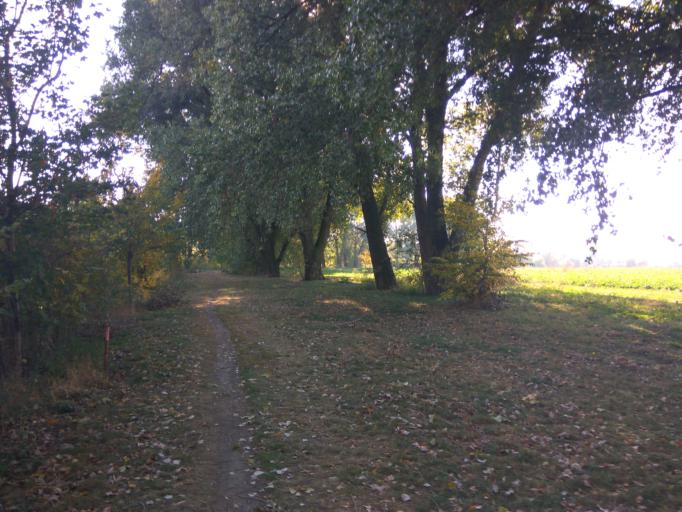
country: CZ
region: Central Bohemia
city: Hovorcovice
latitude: 50.1587
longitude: 14.5377
